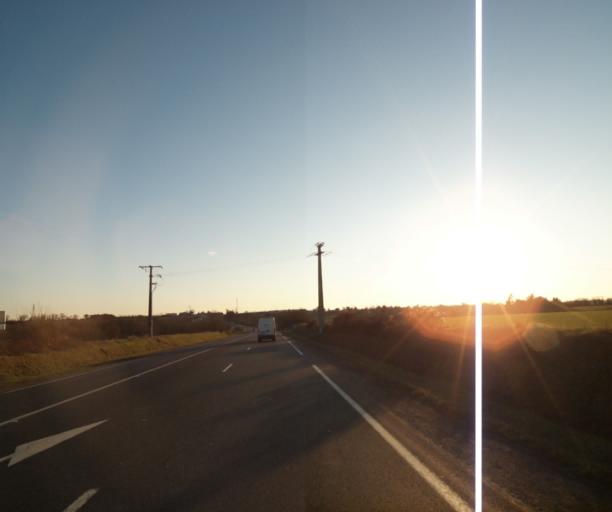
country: FR
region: Poitou-Charentes
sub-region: Departement des Deux-Sevres
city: Echire
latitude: 46.3581
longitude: -0.4355
